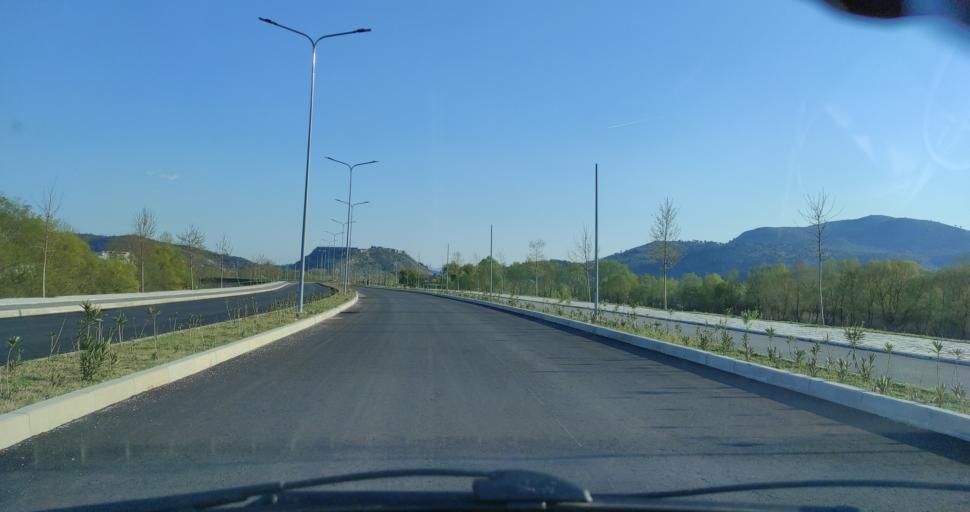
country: AL
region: Shkoder
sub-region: Rrethi i Shkodres
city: Shkoder
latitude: 42.0680
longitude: 19.4893
